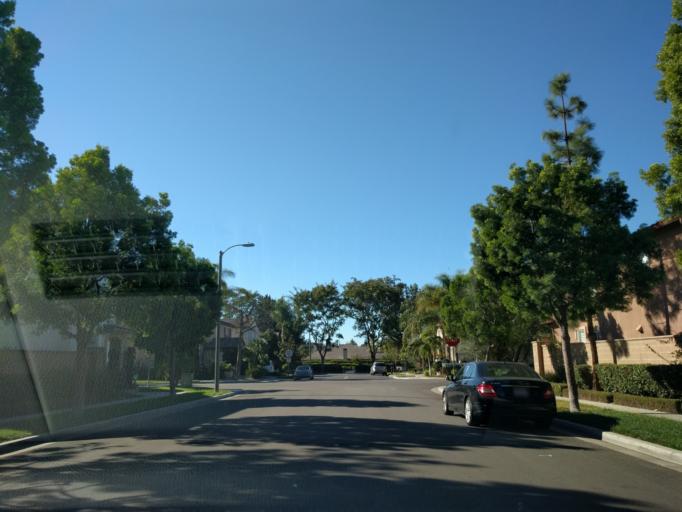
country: US
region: California
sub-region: Orange County
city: North Tustin
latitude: 33.7234
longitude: -117.7785
